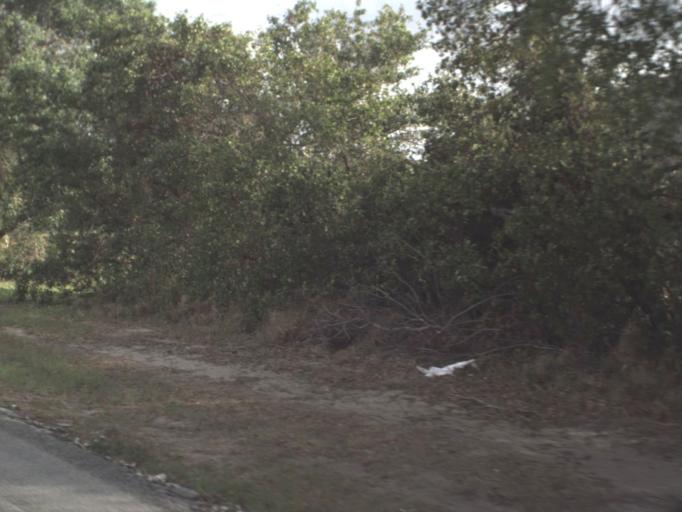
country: US
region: Florida
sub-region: Brevard County
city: Mims
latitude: 28.6565
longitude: -80.8416
